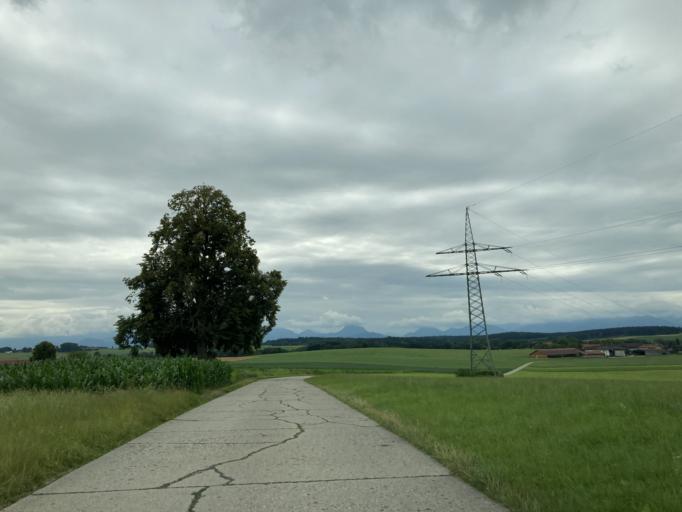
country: DE
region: Bavaria
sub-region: Upper Bavaria
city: Vogtareuth
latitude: 47.9429
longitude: 12.1764
